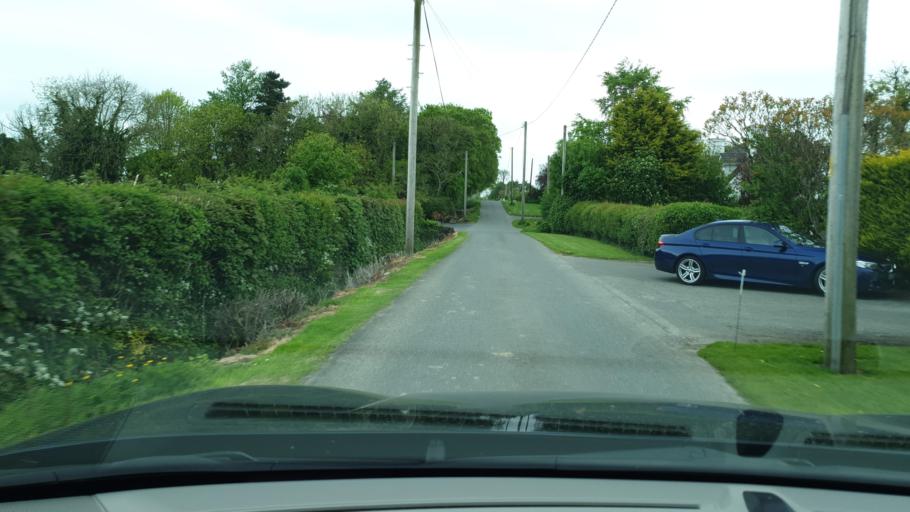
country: IE
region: Leinster
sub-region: An Mhi
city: Ratoath
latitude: 53.4958
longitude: -6.4911
